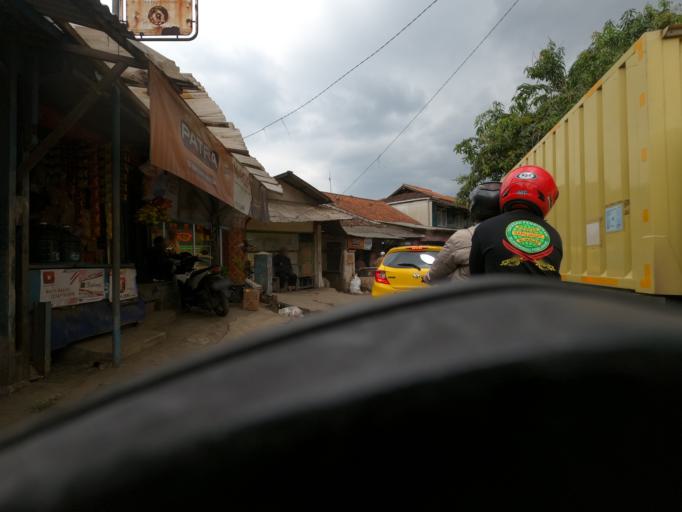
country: ID
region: West Java
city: Padalarang
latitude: -6.8438
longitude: 107.4998
